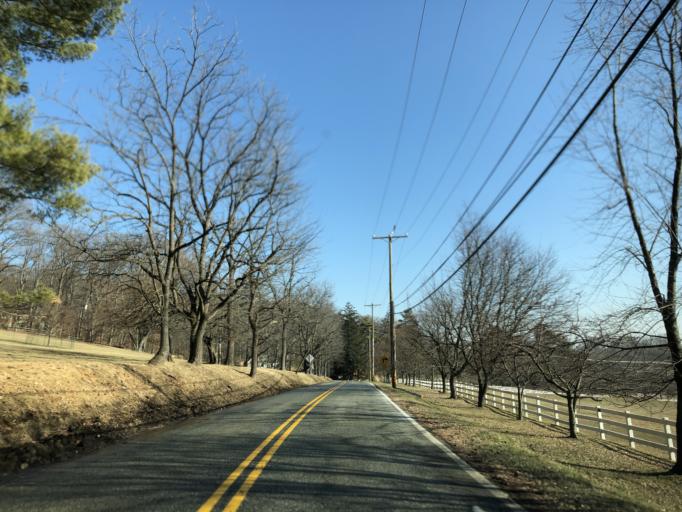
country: US
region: Pennsylvania
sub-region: Chester County
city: Chesterbrook
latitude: 40.0802
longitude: -75.4881
